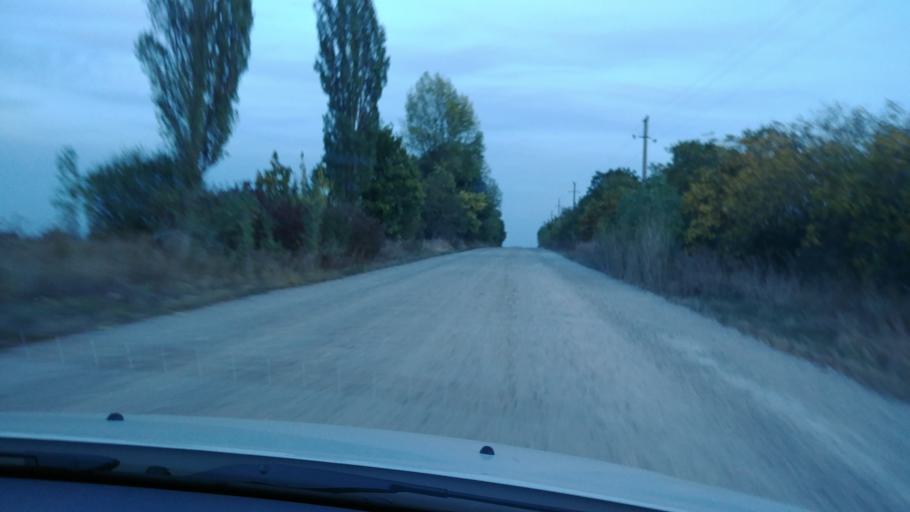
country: MD
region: Rezina
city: Saharna
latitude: 47.6704
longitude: 28.9419
